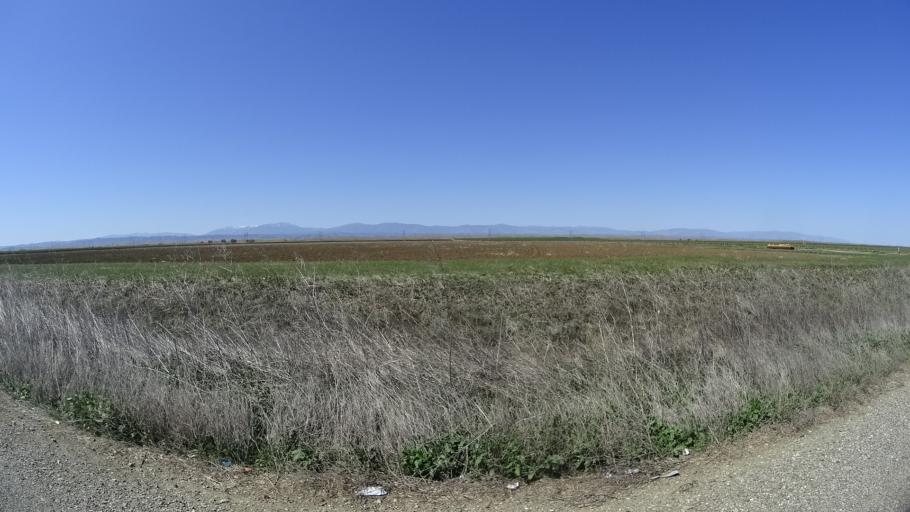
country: US
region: California
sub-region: Glenn County
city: Willows
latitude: 39.5597
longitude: -122.2495
